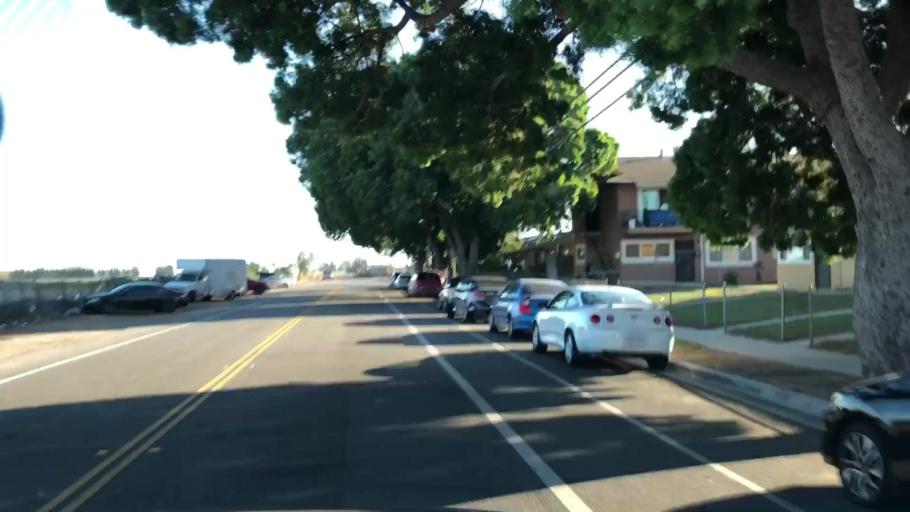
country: US
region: California
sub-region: Ventura County
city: Port Hueneme
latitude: 34.1560
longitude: -119.1489
